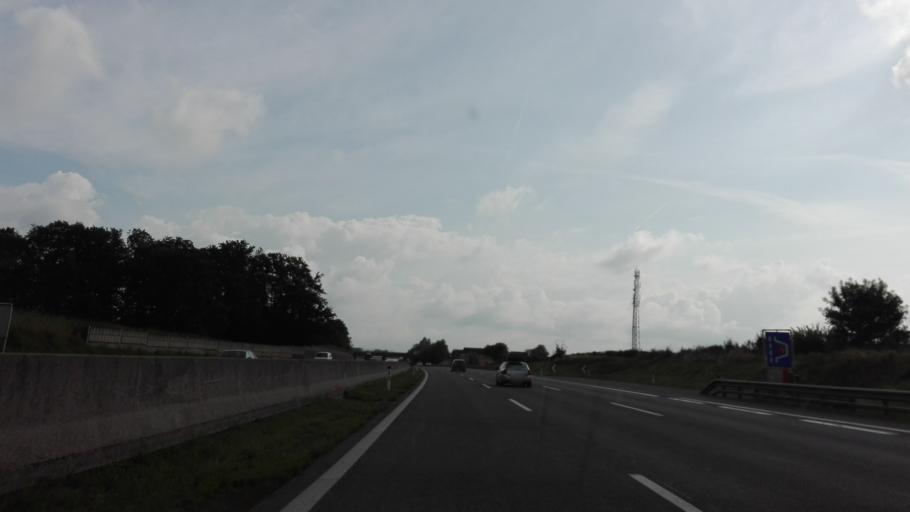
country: AT
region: Lower Austria
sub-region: Politischer Bezirk Amstetten
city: Amstetten
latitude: 48.1383
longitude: 14.8436
